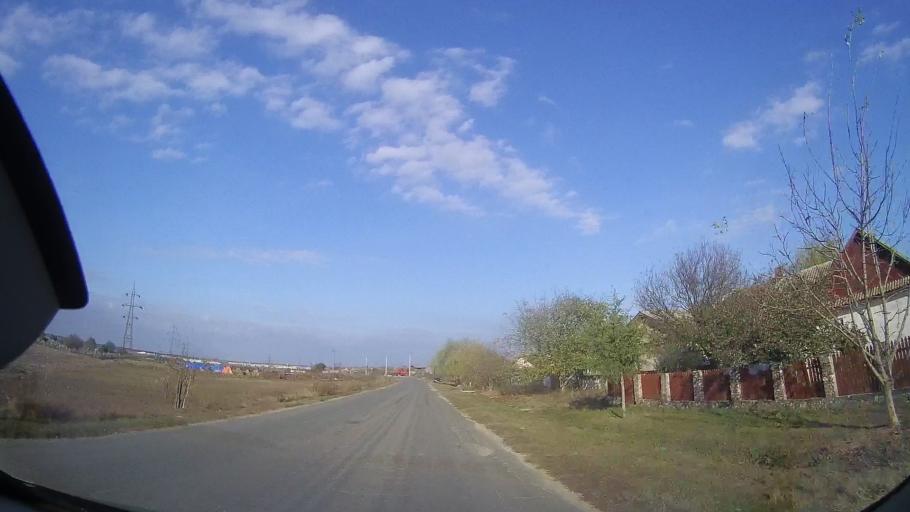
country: RO
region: Constanta
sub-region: Comuna Limanu
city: Limanu
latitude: 43.7977
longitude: 28.5206
